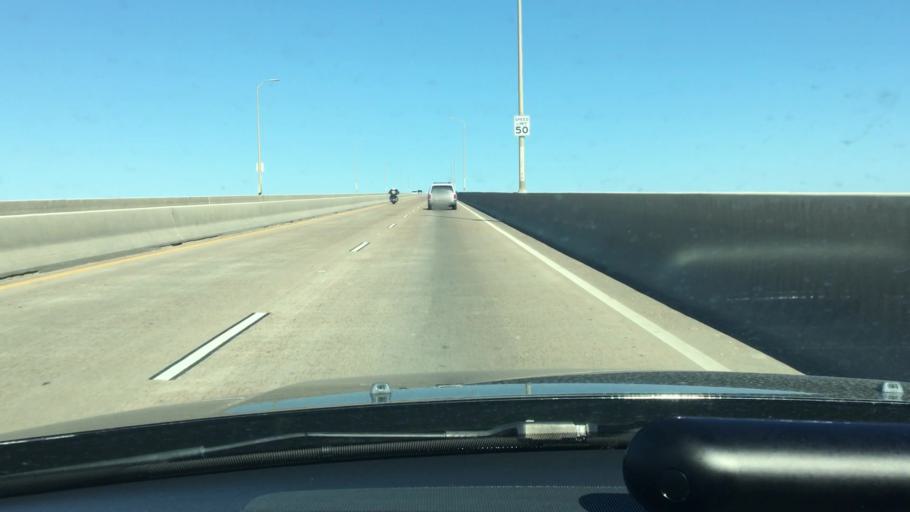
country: US
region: Texas
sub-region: Harris County
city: Deer Park
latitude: 29.7299
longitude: -95.1468
